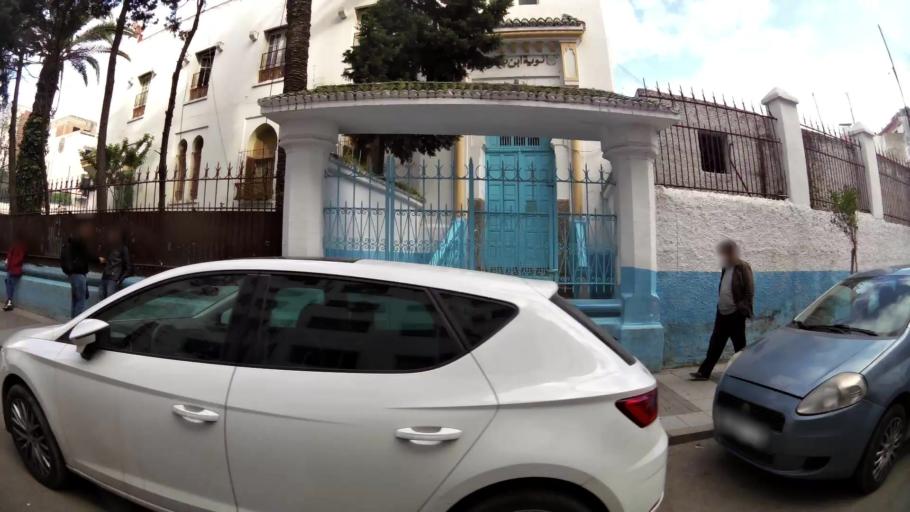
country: MA
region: Tanger-Tetouan
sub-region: Tanger-Assilah
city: Tangier
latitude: 35.7774
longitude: -5.8111
